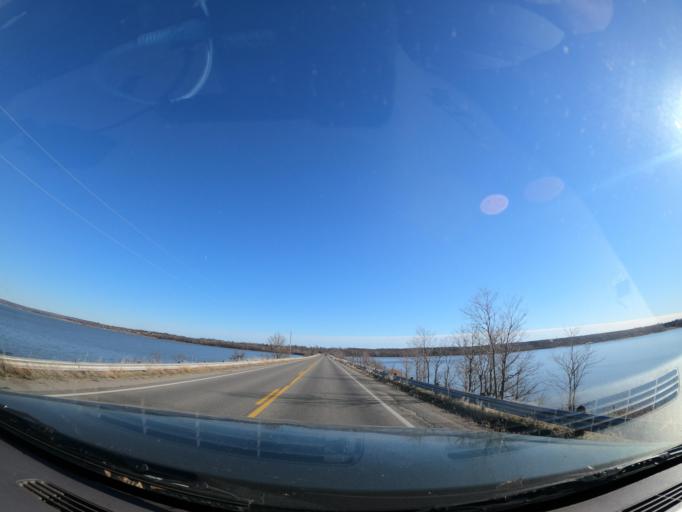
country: US
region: Oklahoma
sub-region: McIntosh County
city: Eufaula
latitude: 35.2443
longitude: -95.5626
